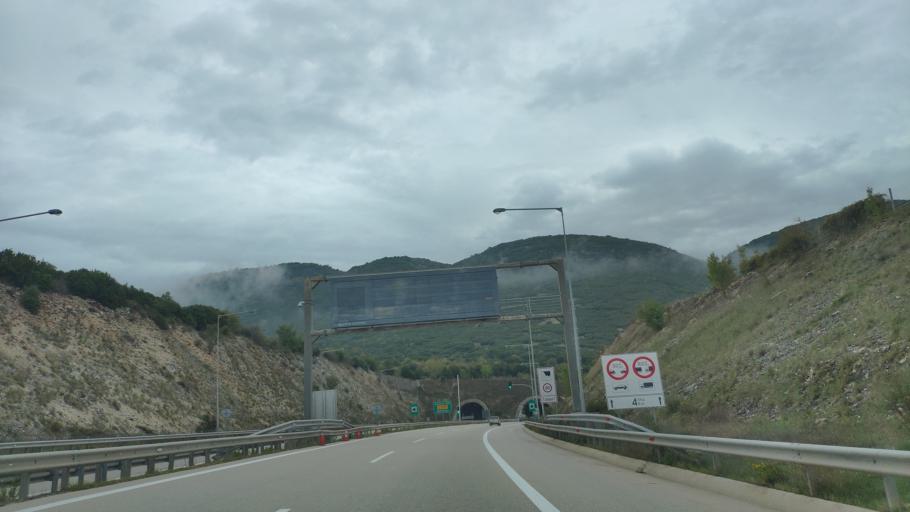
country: GR
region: Epirus
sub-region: Nomos Ioanninon
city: Pedini
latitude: 39.5662
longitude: 20.7802
